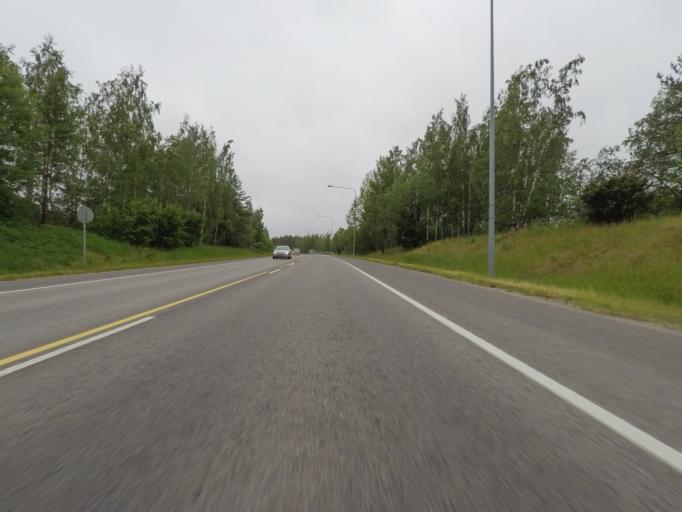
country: FI
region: Varsinais-Suomi
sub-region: Turku
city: Raisio
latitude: 60.4611
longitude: 22.1757
